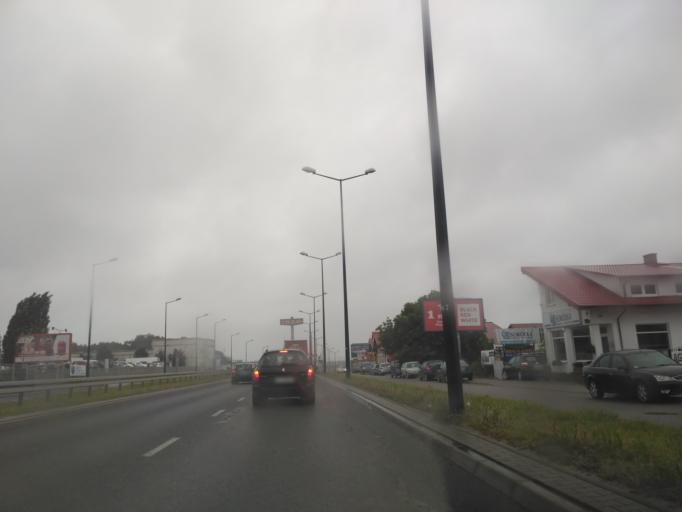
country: PL
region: Lublin Voivodeship
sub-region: Powiat lubelski
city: Lublin
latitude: 51.2770
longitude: 22.5742
